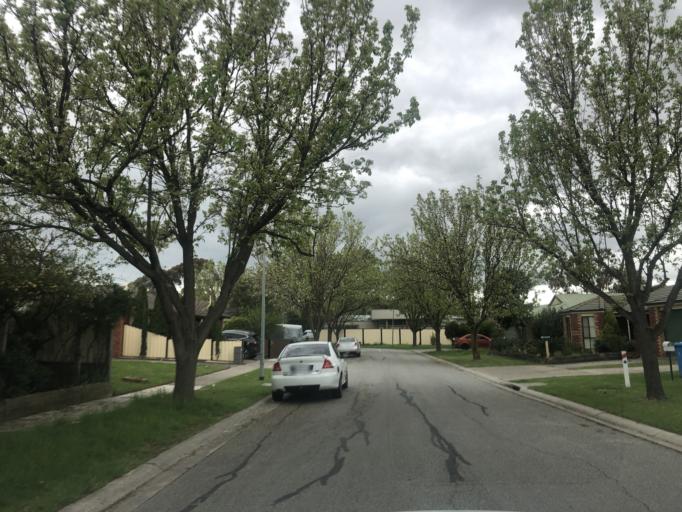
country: AU
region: Victoria
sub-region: Casey
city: Doveton
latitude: -37.9798
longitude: 145.2385
